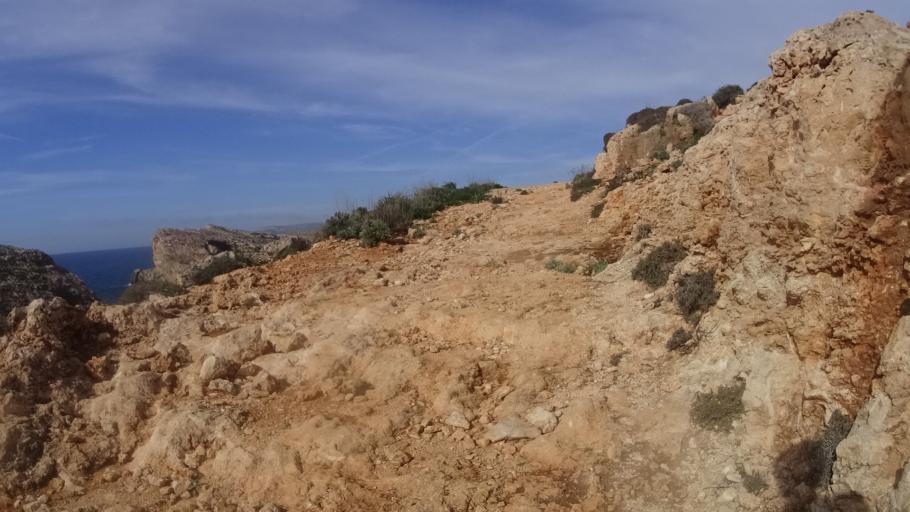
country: MT
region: Il-Qala
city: Qala
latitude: 36.0107
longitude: 14.3277
